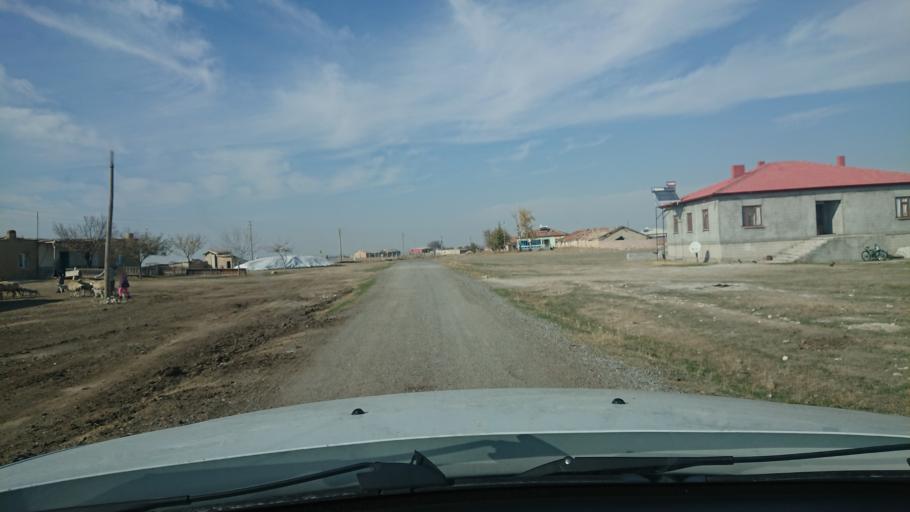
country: TR
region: Aksaray
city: Sultanhani
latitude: 38.2563
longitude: 33.4781
